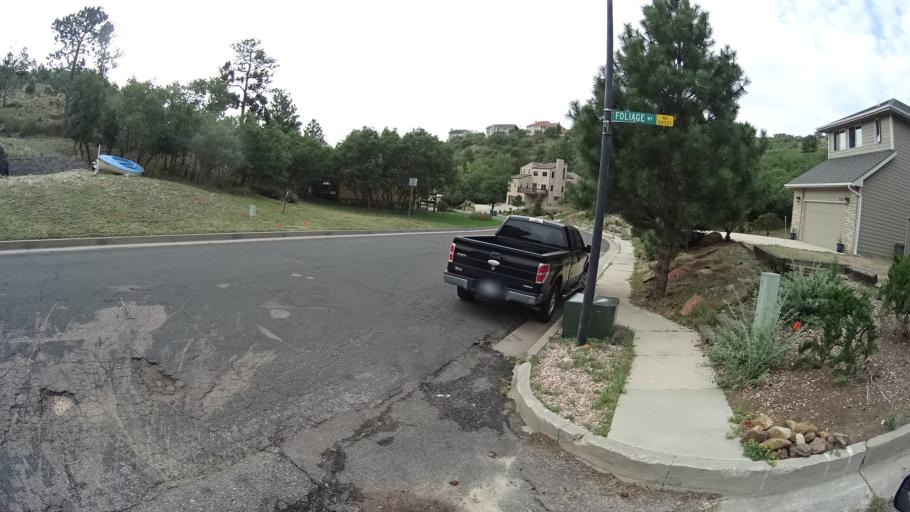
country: US
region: Colorado
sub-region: El Paso County
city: Air Force Academy
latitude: 38.9338
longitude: -104.8595
